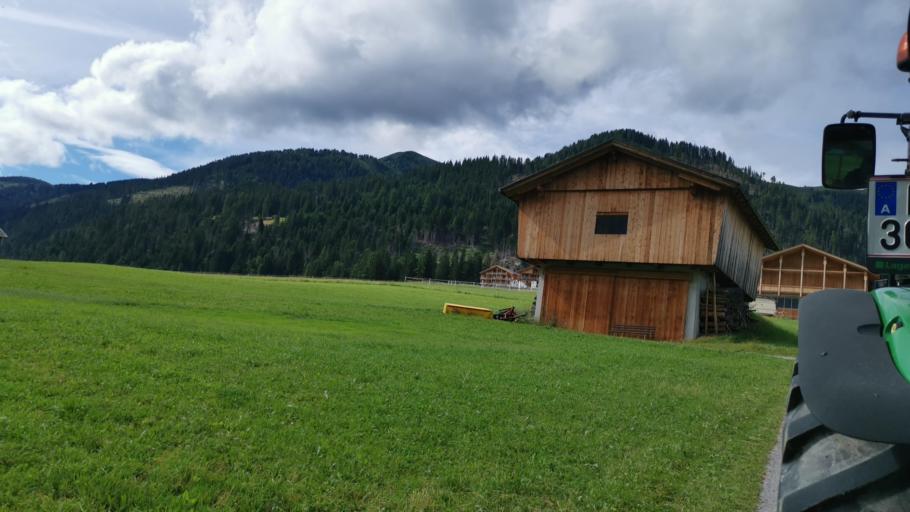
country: AT
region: Tyrol
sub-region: Politischer Bezirk Lienz
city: Obertilliach
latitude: 46.7064
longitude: 12.6113
